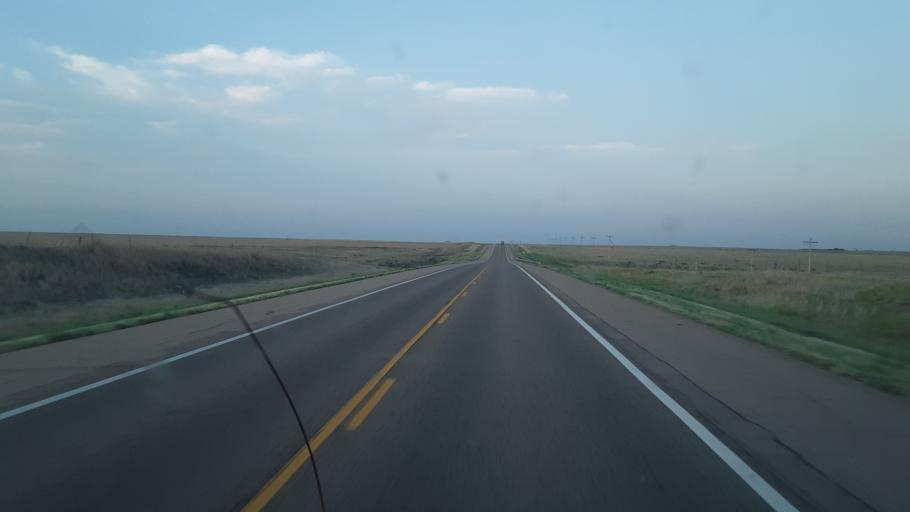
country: US
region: Kansas
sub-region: Kearny County
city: Lakin
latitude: 37.9440
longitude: -101.4397
